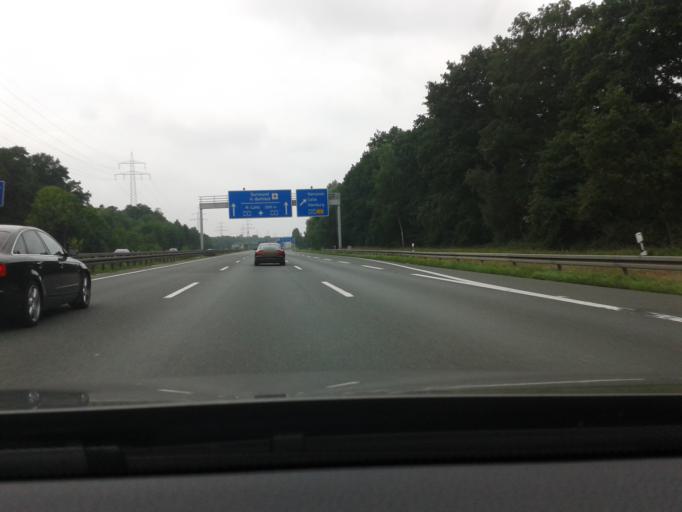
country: DE
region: Lower Saxony
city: Isernhagen Farster Bauerschaft
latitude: 52.4075
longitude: 9.8587
